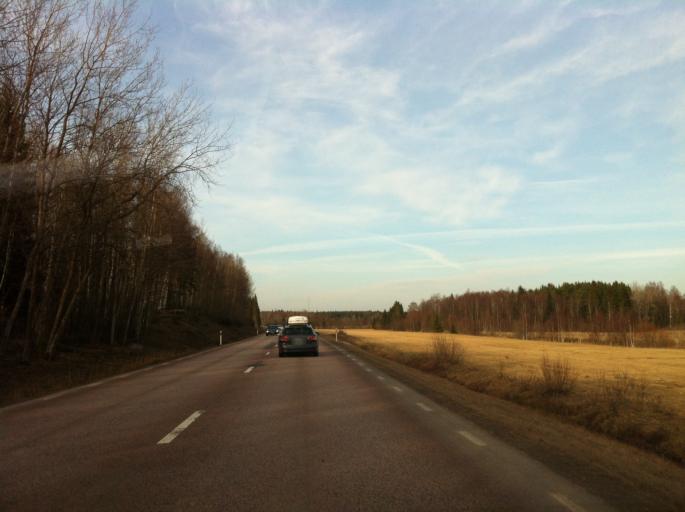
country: SE
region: Vaermland
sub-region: Kristinehamns Kommun
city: Bjorneborg
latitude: 59.2116
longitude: 14.1835
